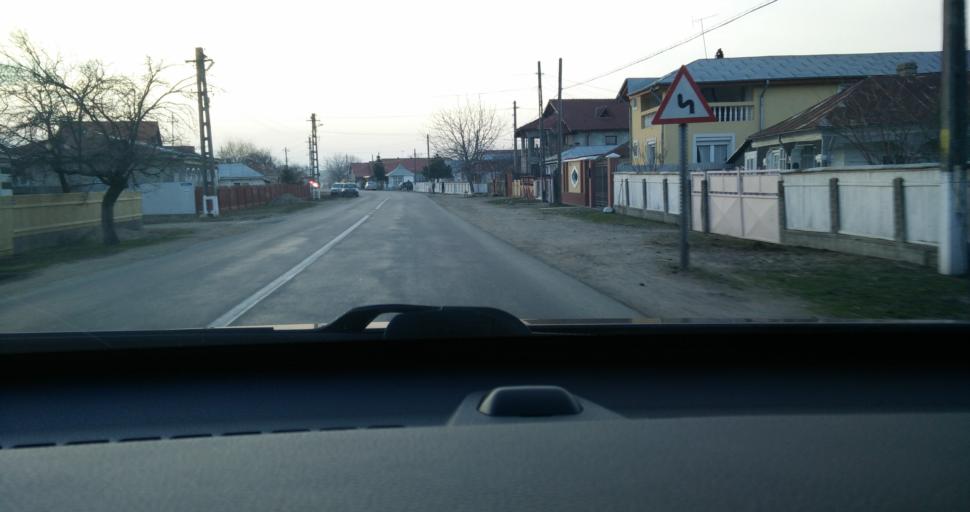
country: RO
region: Vrancea
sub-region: Comuna Rastoaca
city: Rastoaca
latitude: 45.6564
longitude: 27.2935
